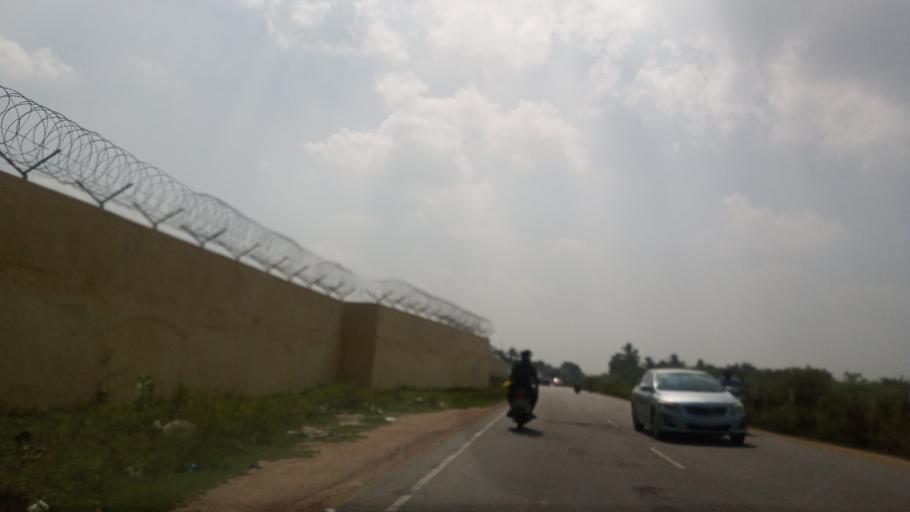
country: IN
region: Tamil Nadu
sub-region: Vellore
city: Arakkonam
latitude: 13.0612
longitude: 79.6738
